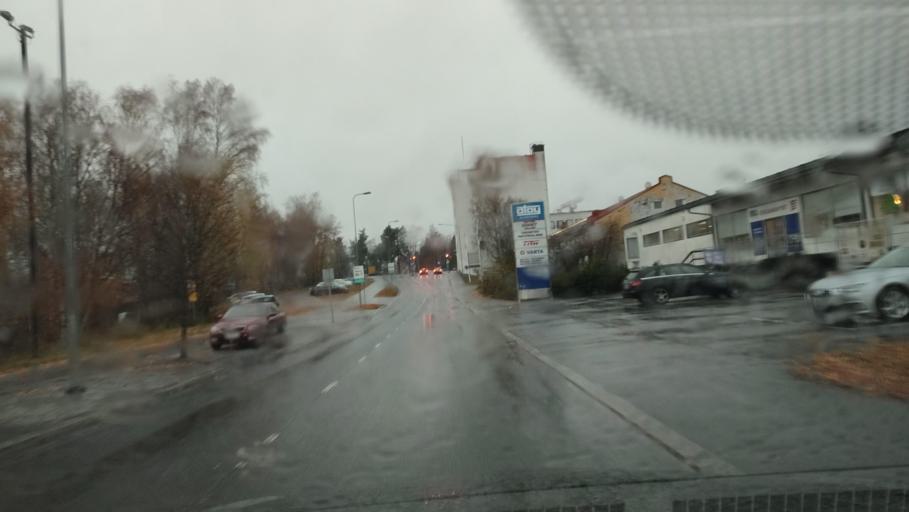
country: FI
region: Ostrobothnia
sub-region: Vaasa
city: Vaasa
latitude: 63.0968
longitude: 21.6276
